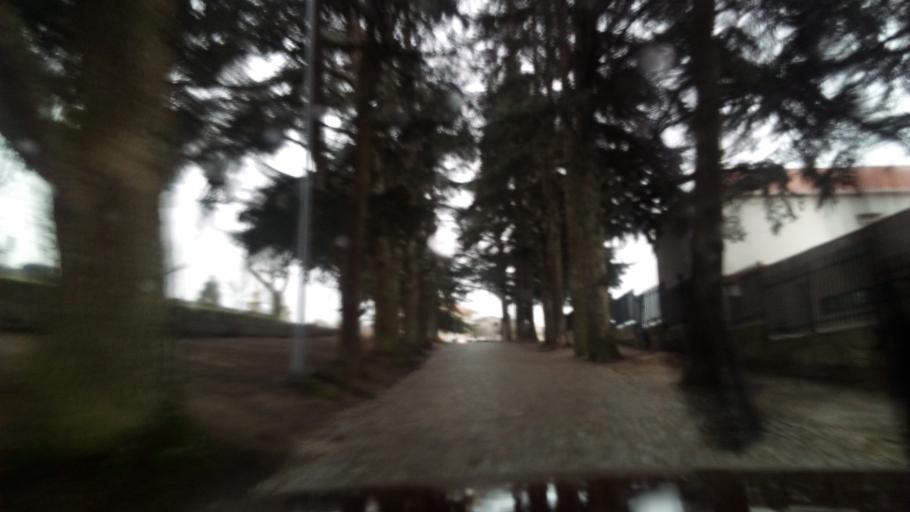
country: PT
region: Guarda
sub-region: Celorico da Beira
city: Celorico da Beira
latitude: 40.6342
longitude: -7.3936
